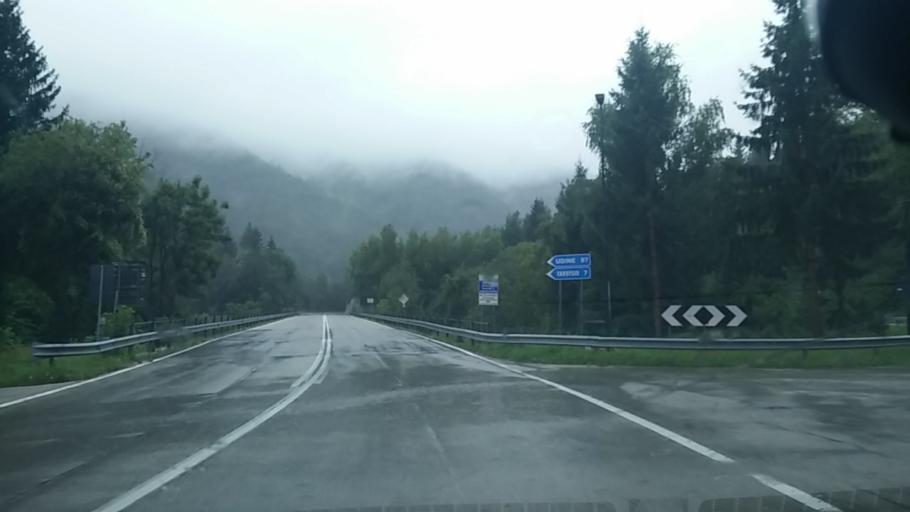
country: AT
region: Carinthia
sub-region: Politischer Bezirk Villach Land
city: Hohenthurn
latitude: 46.5333
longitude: 13.6387
